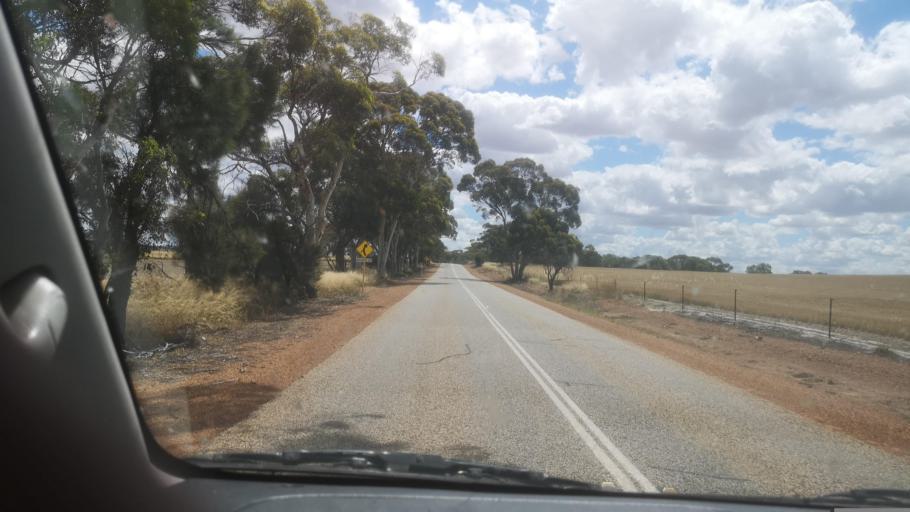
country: AU
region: Western Australia
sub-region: Beverley
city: Beverley
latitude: -31.9899
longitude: 117.1064
